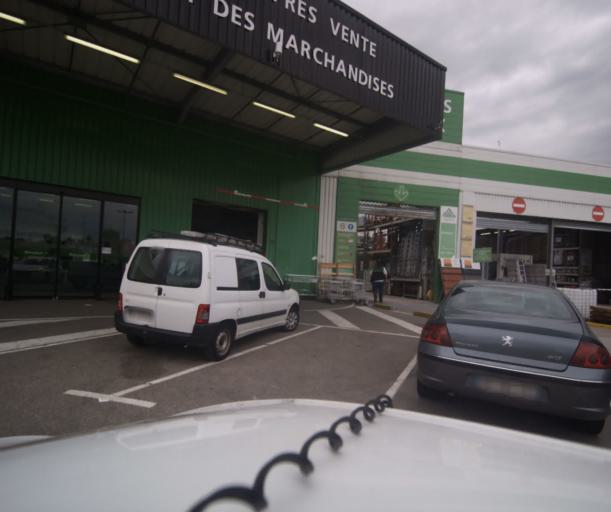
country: FR
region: Franche-Comte
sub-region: Departement du Doubs
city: Franois
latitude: 47.2156
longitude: 5.9434
